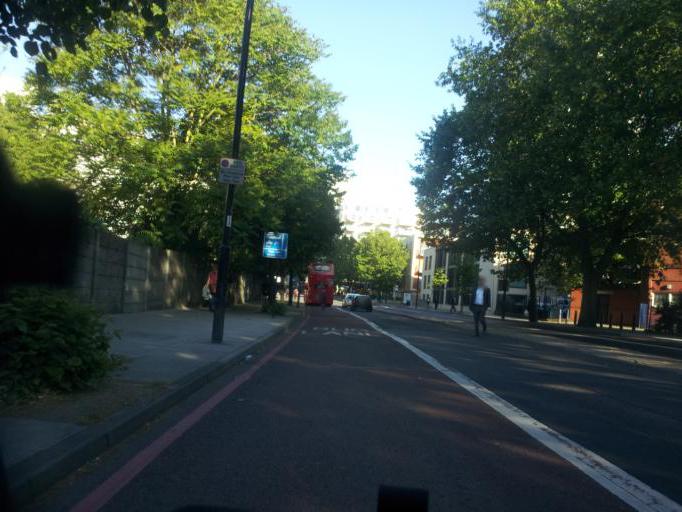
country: GB
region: England
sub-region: Greater London
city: City of London
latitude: 51.4995
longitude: -0.0719
